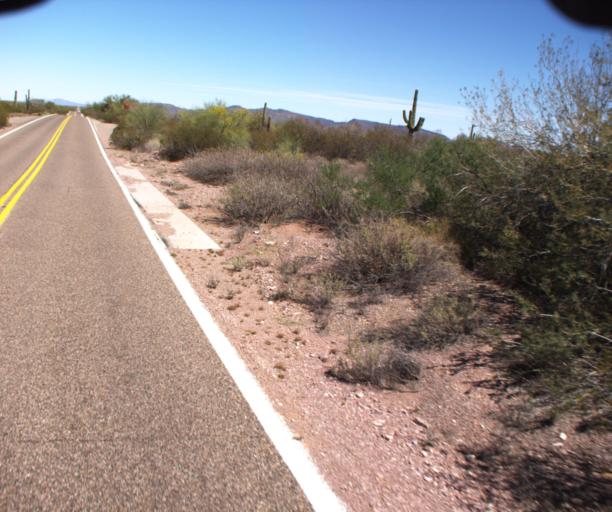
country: US
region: Arizona
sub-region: Pima County
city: Ajo
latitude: 32.1222
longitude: -112.7686
